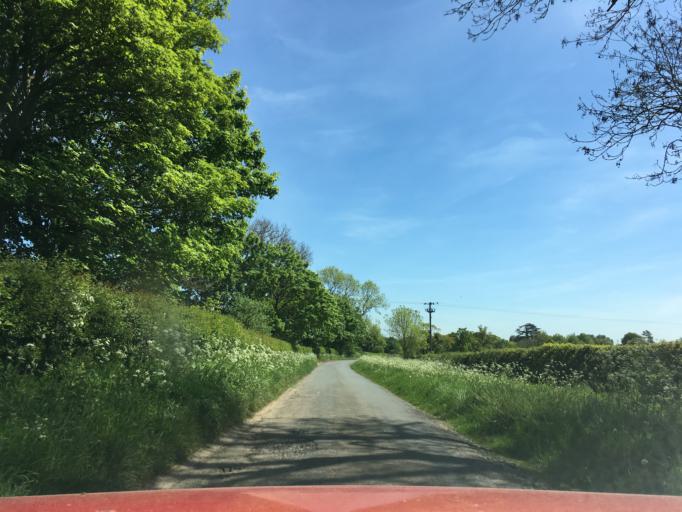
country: GB
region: England
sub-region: Gloucestershire
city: Coates
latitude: 51.6812
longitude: -1.9966
